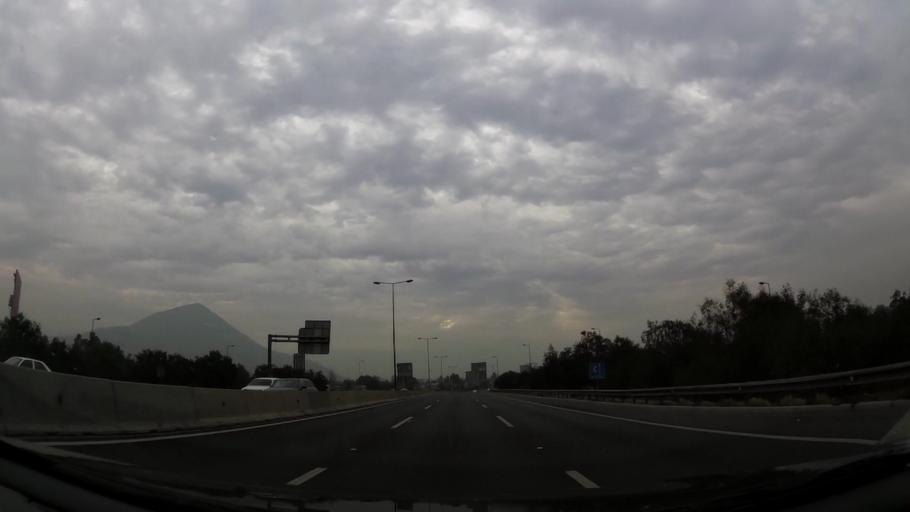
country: CL
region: Santiago Metropolitan
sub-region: Provincia de Santiago
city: Lo Prado
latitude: -33.4107
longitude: -70.7225
